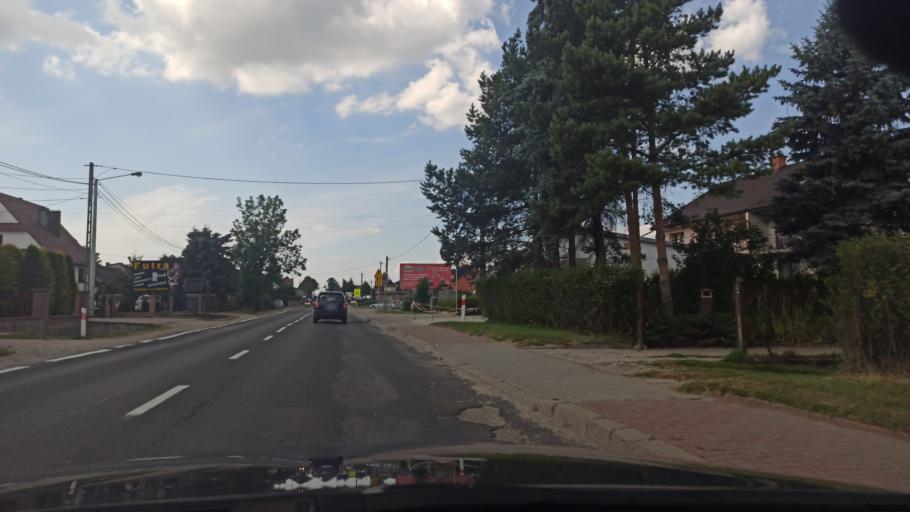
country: PL
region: Lesser Poland Voivodeship
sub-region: Powiat nowotarski
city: Ostrowsko
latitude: 49.4747
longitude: 20.1041
